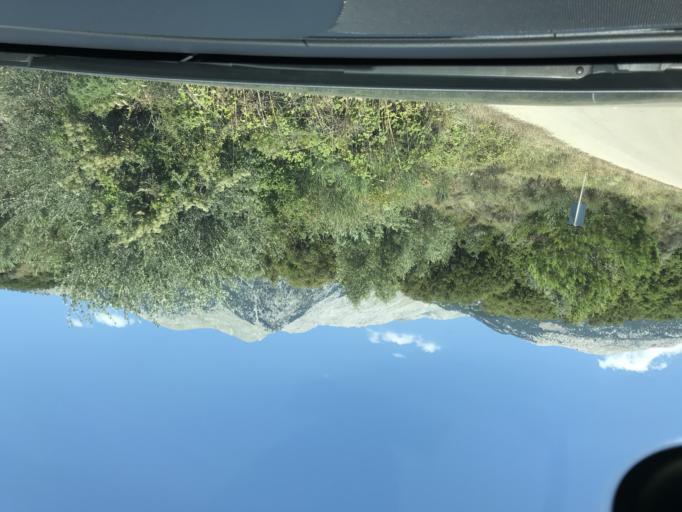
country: GR
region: Central Greece
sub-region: Nomos Fthiotidos
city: Kato Tithorea
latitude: 38.5126
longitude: 22.7218
